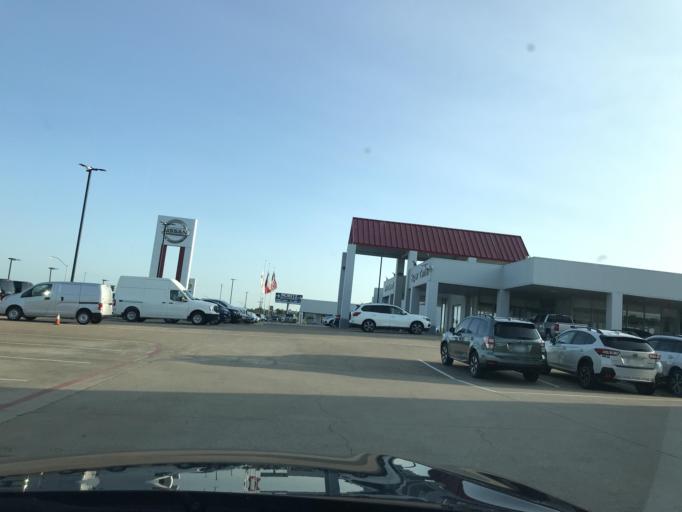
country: US
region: Texas
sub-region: Tarrant County
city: White Settlement
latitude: 32.7200
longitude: -97.4784
